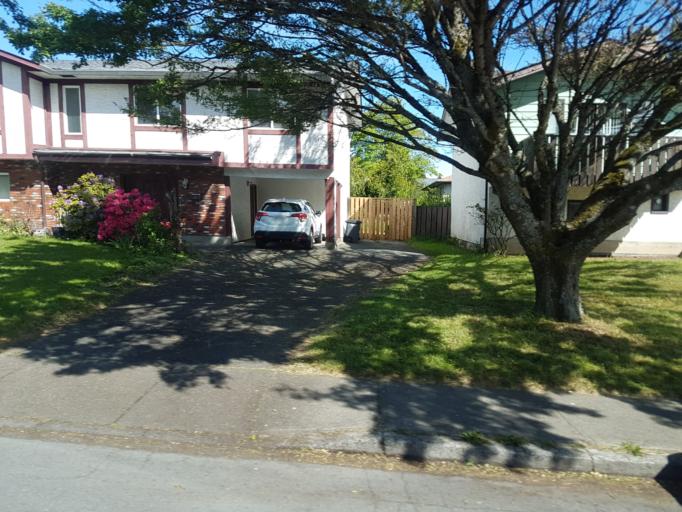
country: CA
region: British Columbia
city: Oak Bay
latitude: 48.4813
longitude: -123.3227
